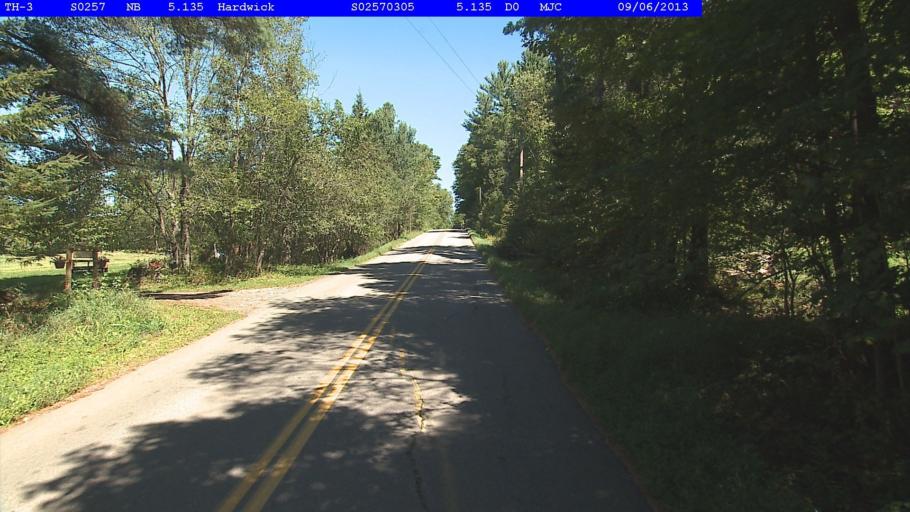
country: US
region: Vermont
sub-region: Caledonia County
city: Hardwick
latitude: 44.5602
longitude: -72.3127
